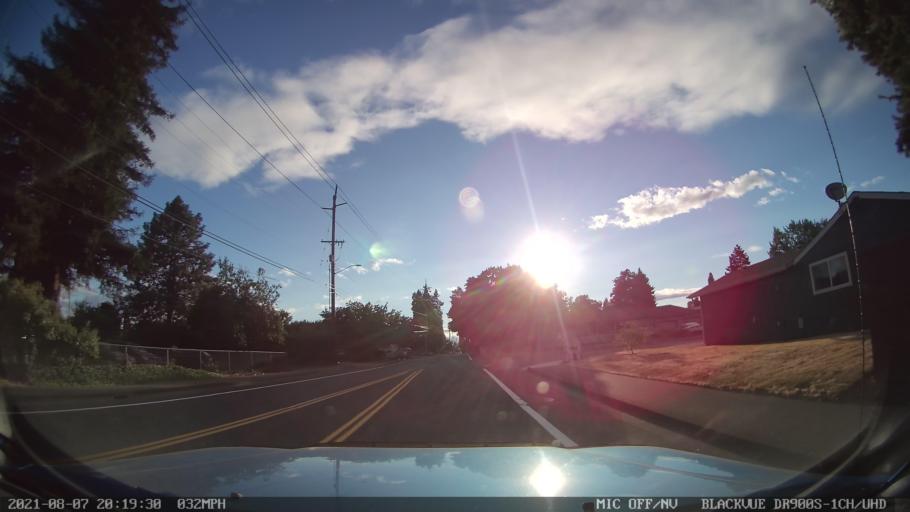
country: US
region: Oregon
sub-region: Marion County
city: Four Corners
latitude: 44.9540
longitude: -122.9934
